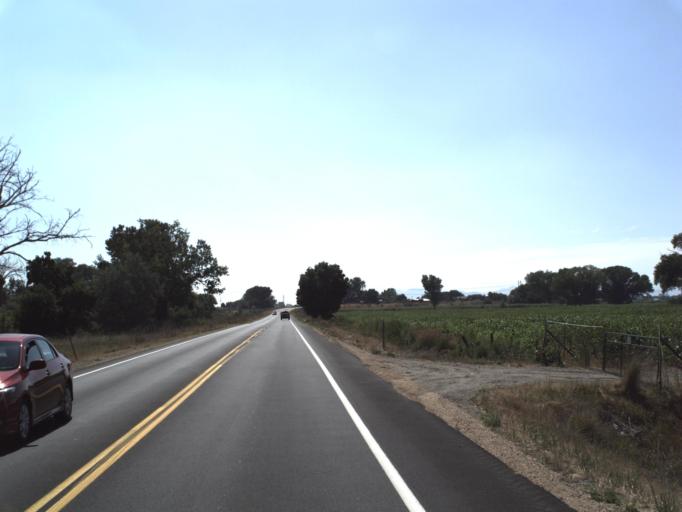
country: US
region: Utah
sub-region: Weber County
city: Marriott-Slaterville
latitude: 41.2452
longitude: -112.0343
